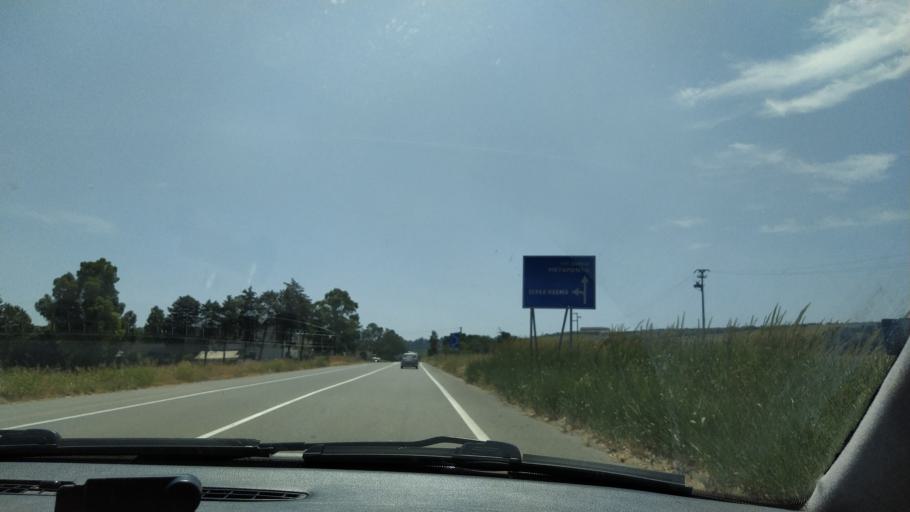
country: IT
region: Basilicate
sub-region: Provincia di Matera
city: Bernalda
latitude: 40.4458
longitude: 16.7787
